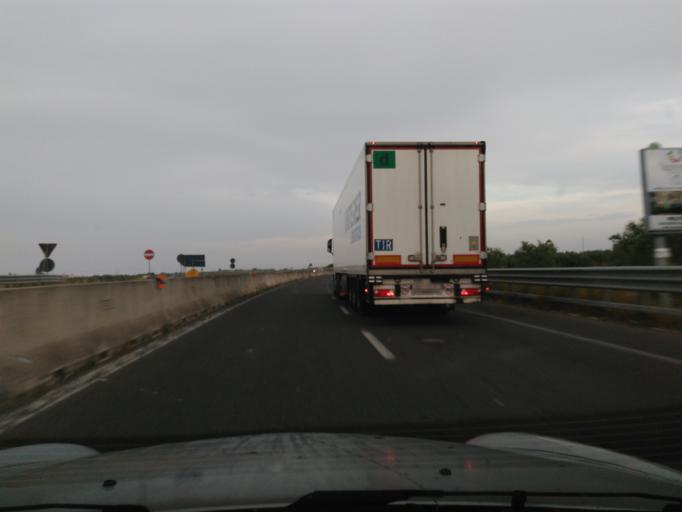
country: IT
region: Apulia
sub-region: Provincia di Bari
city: Giovinazzo
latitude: 41.1838
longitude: 16.6394
